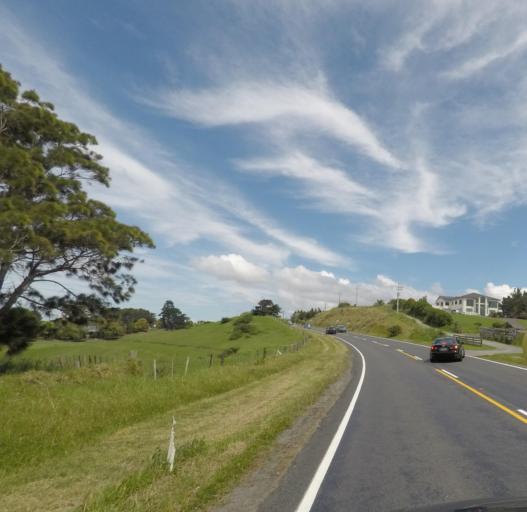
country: NZ
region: Auckland
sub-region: Auckland
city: Rothesay Bay
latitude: -36.6375
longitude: 174.6688
